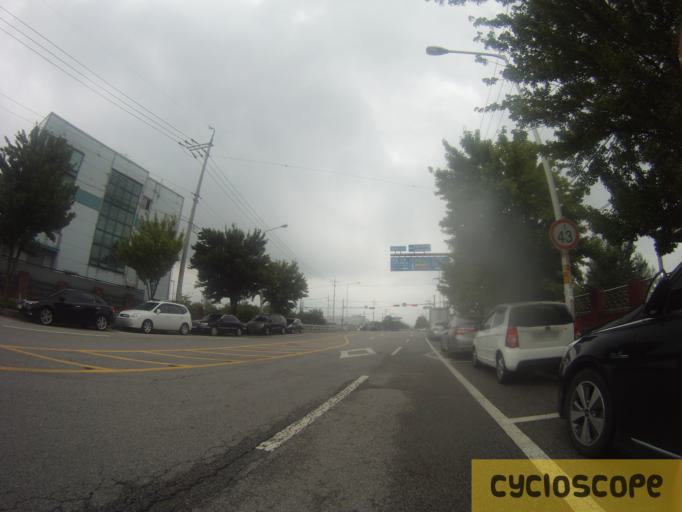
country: KR
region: Gyeonggi-do
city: Hwaseong-si
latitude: 37.0712
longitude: 126.7988
